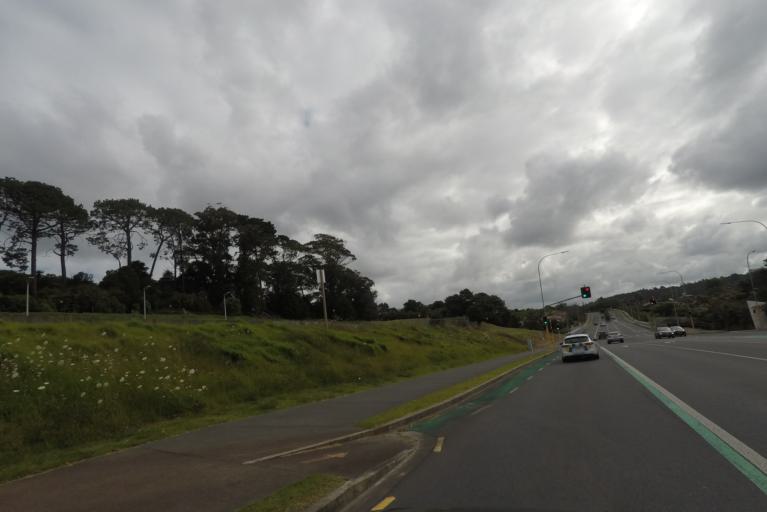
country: NZ
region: Auckland
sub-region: Auckland
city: Rothesay Bay
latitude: -36.7309
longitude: 174.6963
